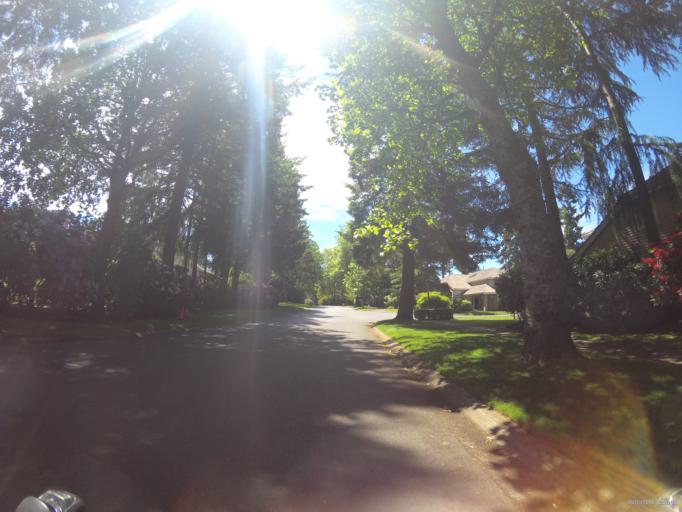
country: US
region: Washington
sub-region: Pierce County
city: University Place
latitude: 47.2004
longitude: -122.5490
